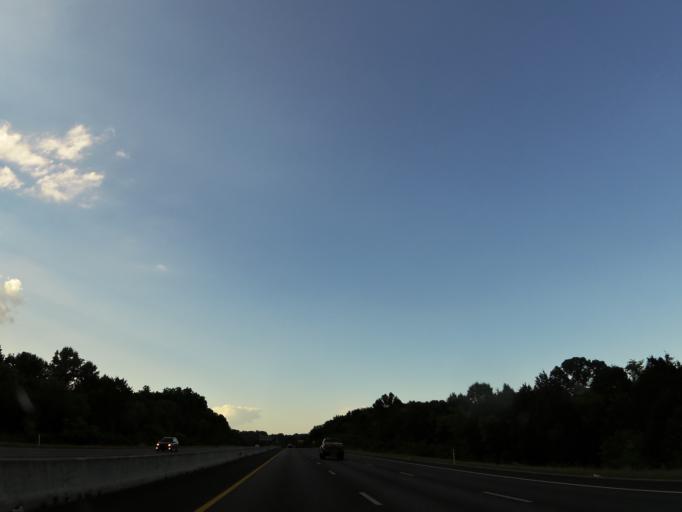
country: US
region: Tennessee
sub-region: Maury County
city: Spring Hill
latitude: 35.7566
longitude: -86.8676
